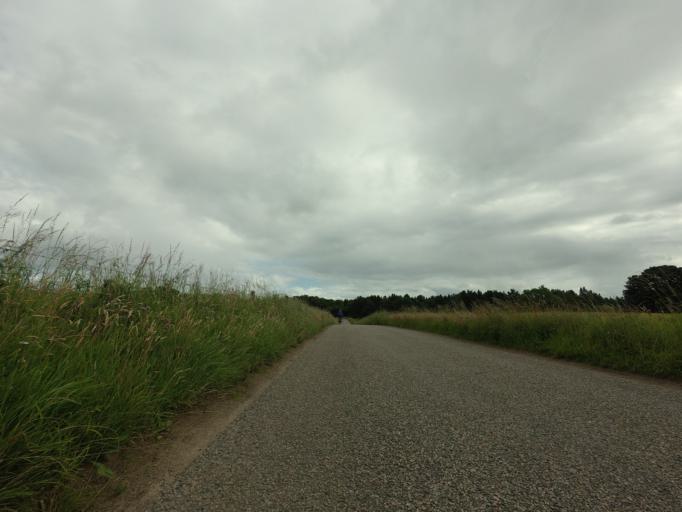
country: GB
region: Scotland
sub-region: Moray
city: Lhanbryd
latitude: 57.6628
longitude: -3.1811
